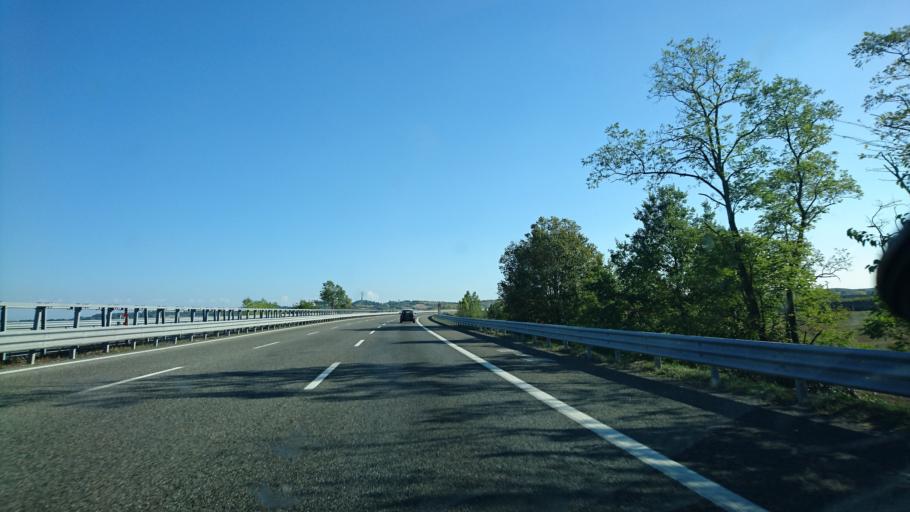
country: IT
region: Piedmont
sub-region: Provincia di Alessandria
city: Mirabello Monferrato
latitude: 45.0316
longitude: 8.5359
